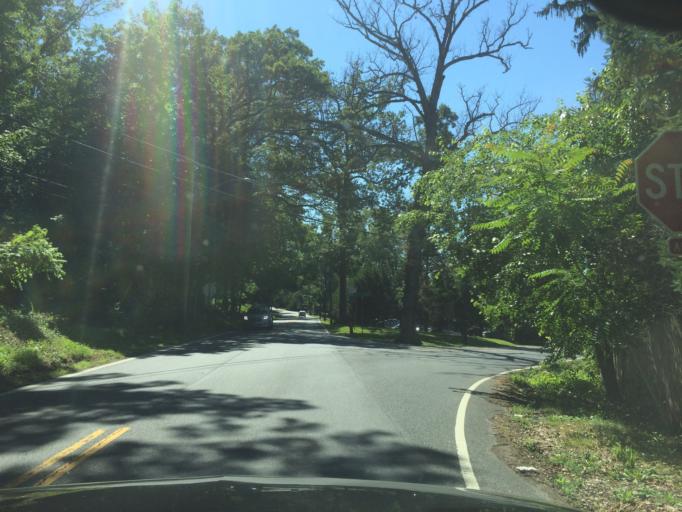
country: US
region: Maryland
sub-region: Baltimore County
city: Garrison
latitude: 39.4043
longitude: -76.7515
